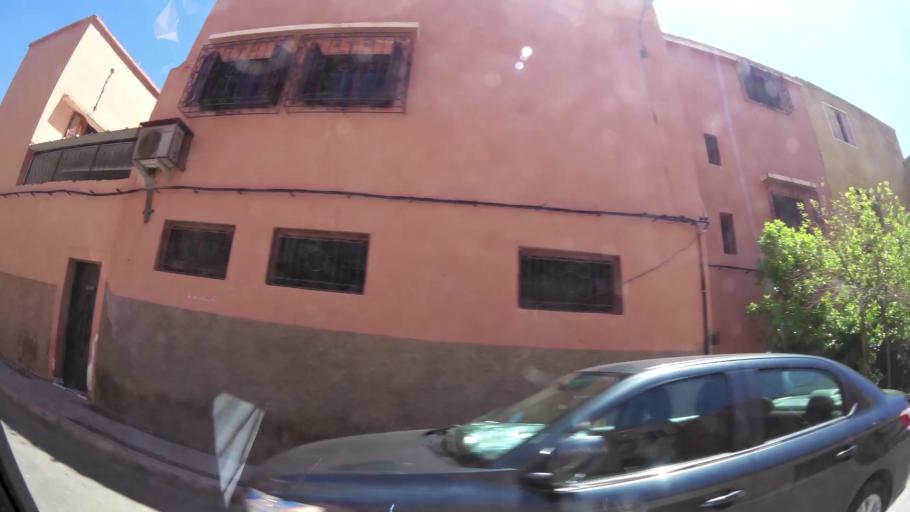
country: MA
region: Marrakech-Tensift-Al Haouz
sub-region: Marrakech
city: Marrakesh
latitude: 31.6512
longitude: -7.9911
